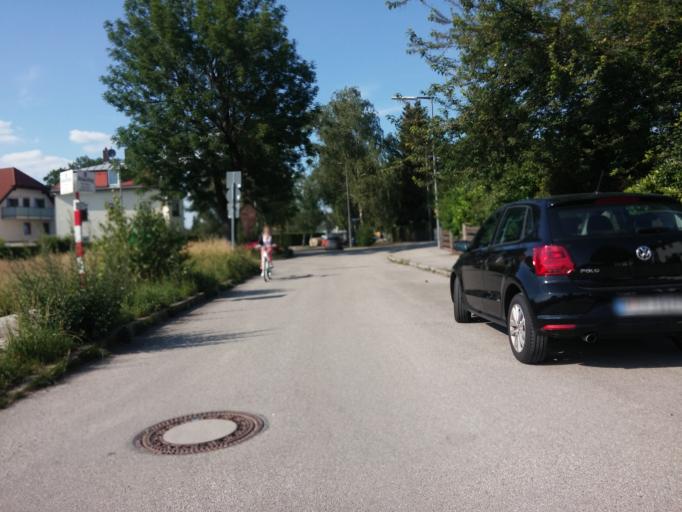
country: DE
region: Bavaria
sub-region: Upper Bavaria
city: Neubiberg
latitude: 48.1264
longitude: 11.6680
